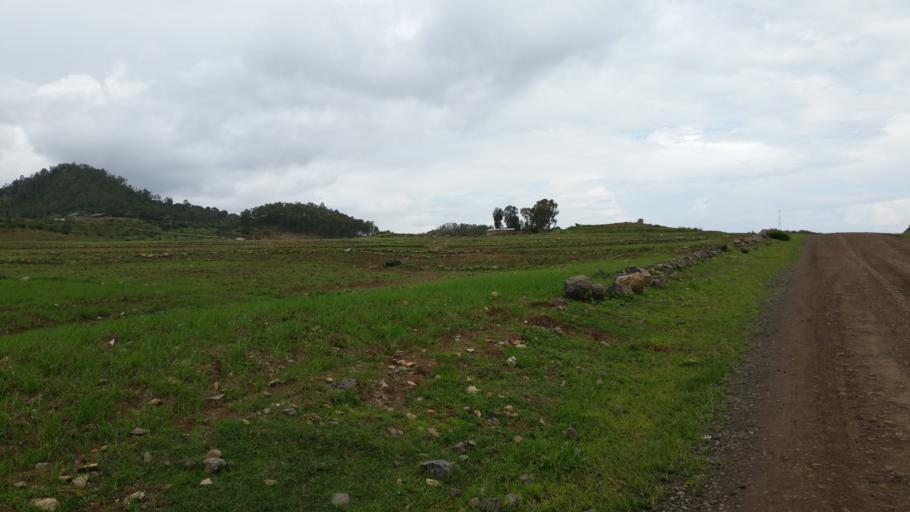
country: ET
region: Tigray
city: Aksum
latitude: 14.1457
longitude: 38.7219
